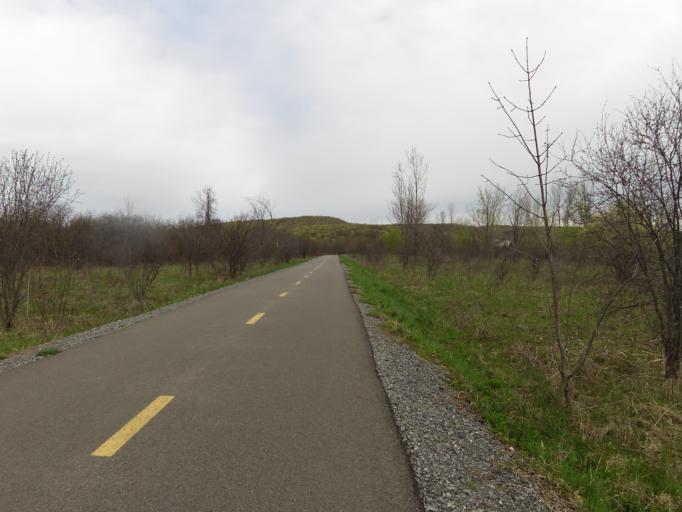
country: CA
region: Quebec
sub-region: Laurentides
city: Sainte-Marthe-sur-le-Lac
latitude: 45.4964
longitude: -74.0003
